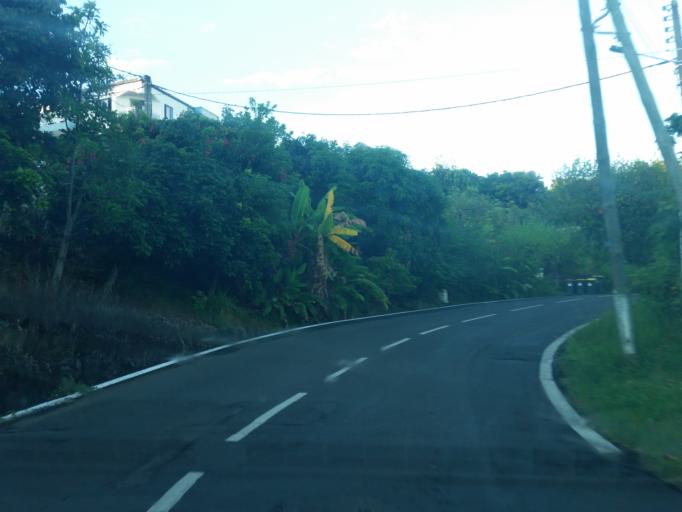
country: RE
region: Reunion
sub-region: Reunion
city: L'Entre-Deux
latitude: -21.2461
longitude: 55.4795
